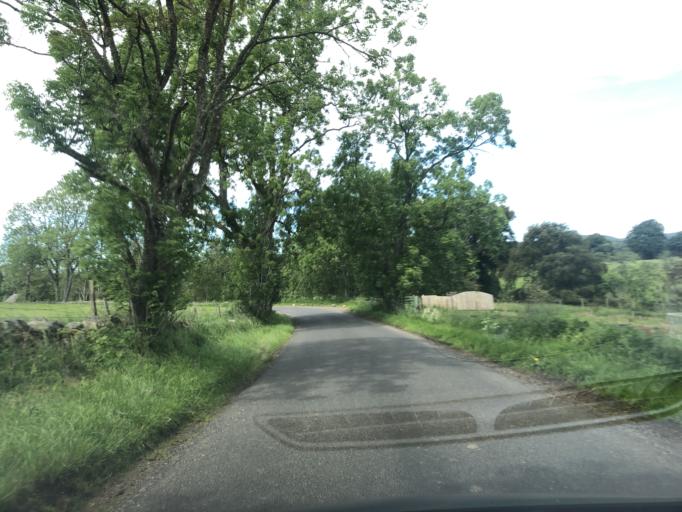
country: GB
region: Scotland
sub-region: Angus
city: Kirriemuir
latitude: 56.7078
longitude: -2.9666
